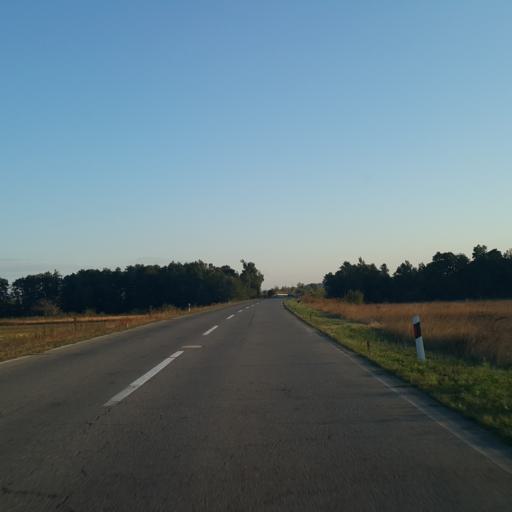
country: RS
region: Central Serbia
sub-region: Borski Okrug
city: Negotin
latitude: 44.1873
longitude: 22.3663
